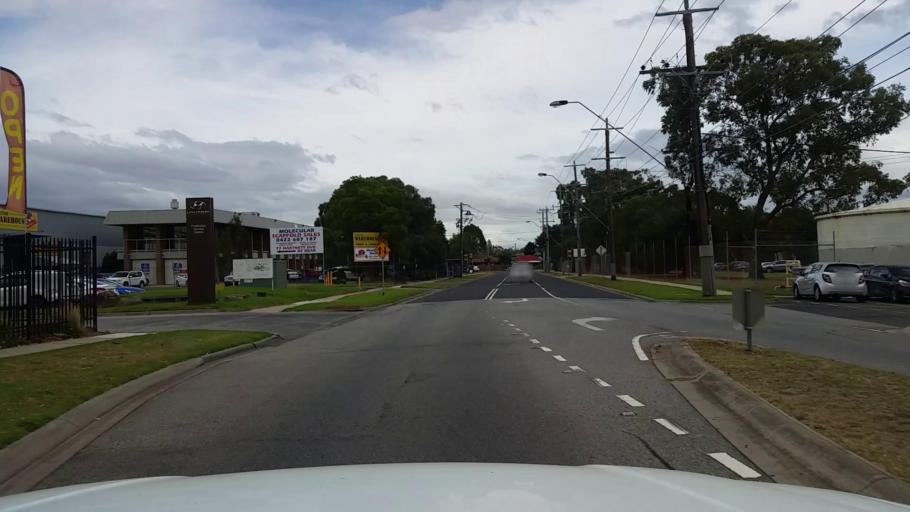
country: AU
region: Victoria
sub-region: Frankston
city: Frankston North
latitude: -38.1172
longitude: 145.1408
